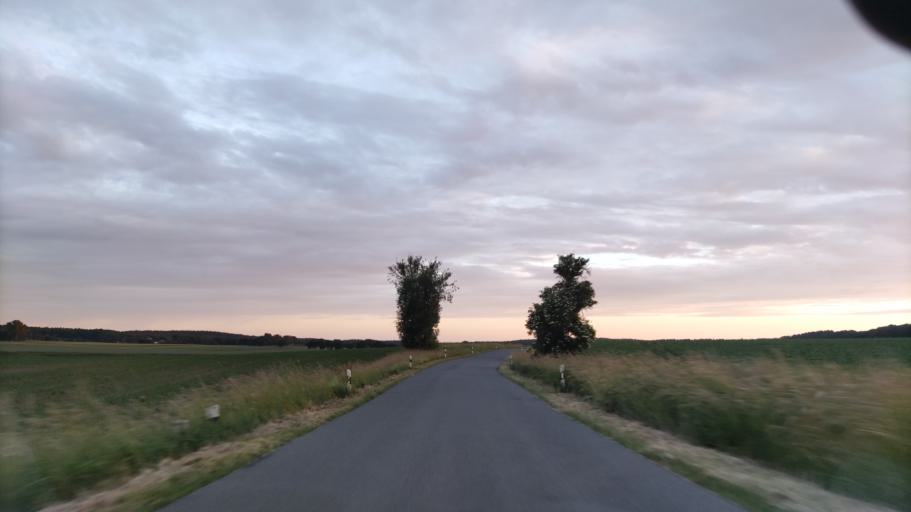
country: DE
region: Lower Saxony
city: Neu Darchau
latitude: 53.1975
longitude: 10.9434
